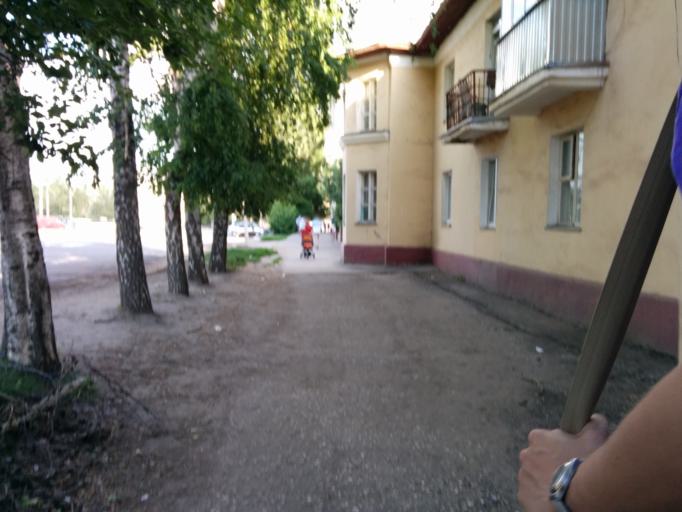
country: RU
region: Tambov
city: Tambov
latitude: 52.7437
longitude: 41.4480
